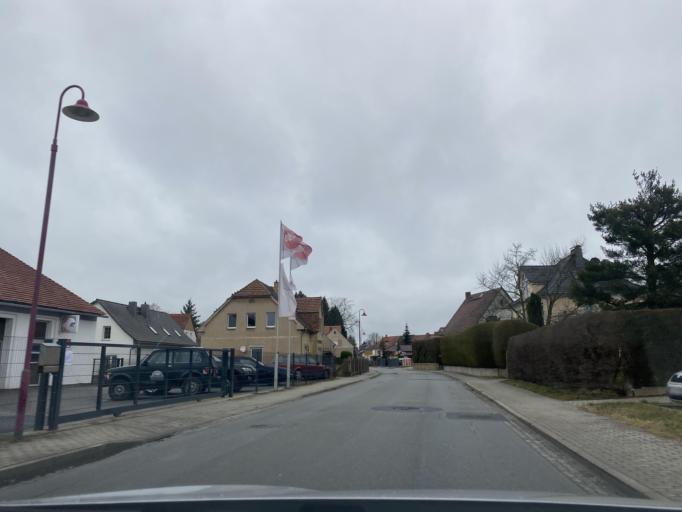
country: DE
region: Saxony
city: Rothenburg
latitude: 51.3342
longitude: 14.9678
